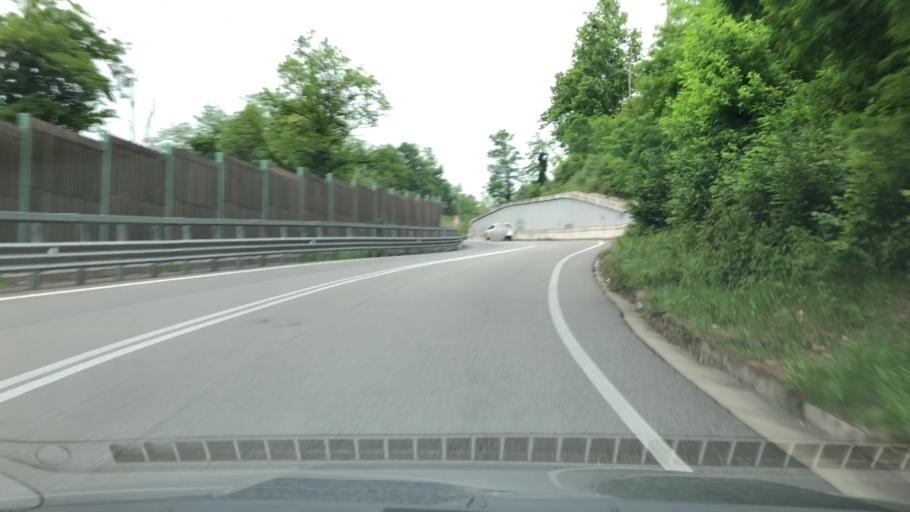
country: IT
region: Lombardy
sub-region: Provincia di Como
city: Casnate Con Bernate
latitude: 45.7693
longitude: 9.0746
